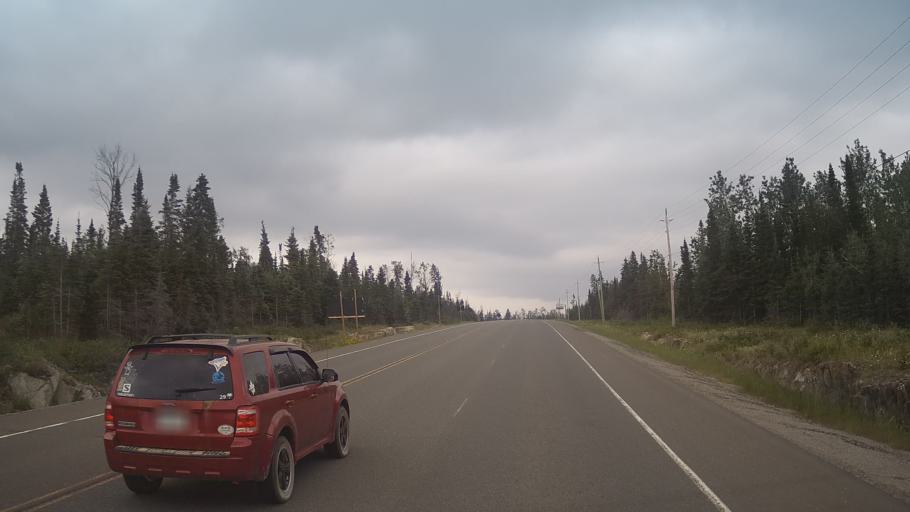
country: CA
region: Ontario
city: Greenstone
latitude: 49.5718
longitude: -87.9750
